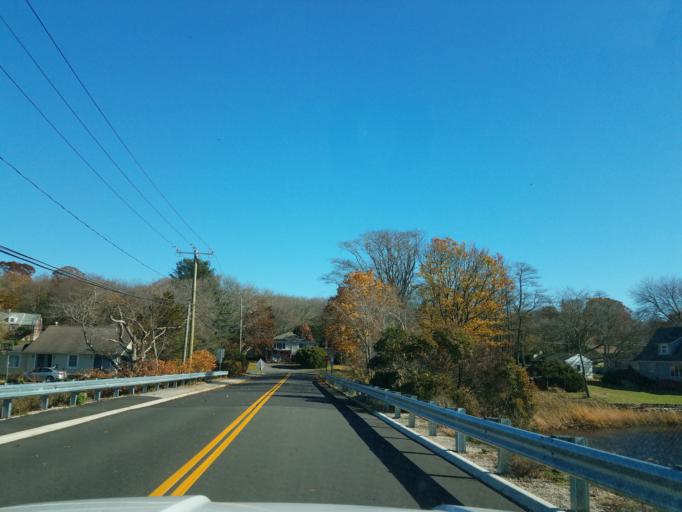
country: US
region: Connecticut
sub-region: New London County
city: Central Waterford
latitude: 41.3193
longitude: -72.1486
